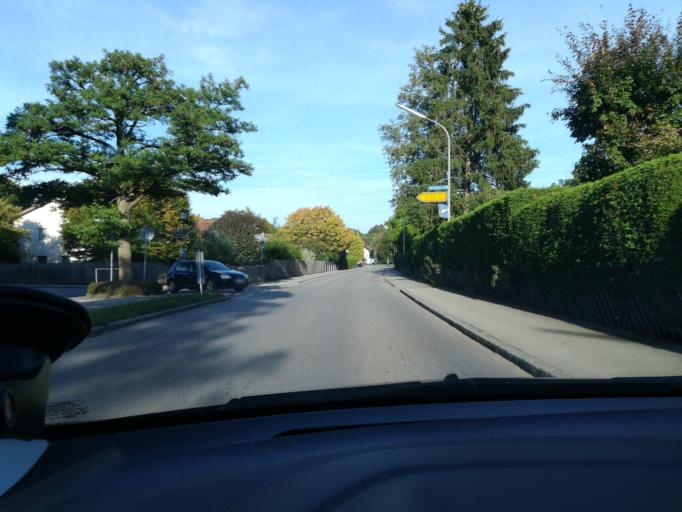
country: DE
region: Bavaria
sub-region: Upper Bavaria
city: Feldkirchen-Westerham
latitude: 47.9073
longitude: 11.8411
